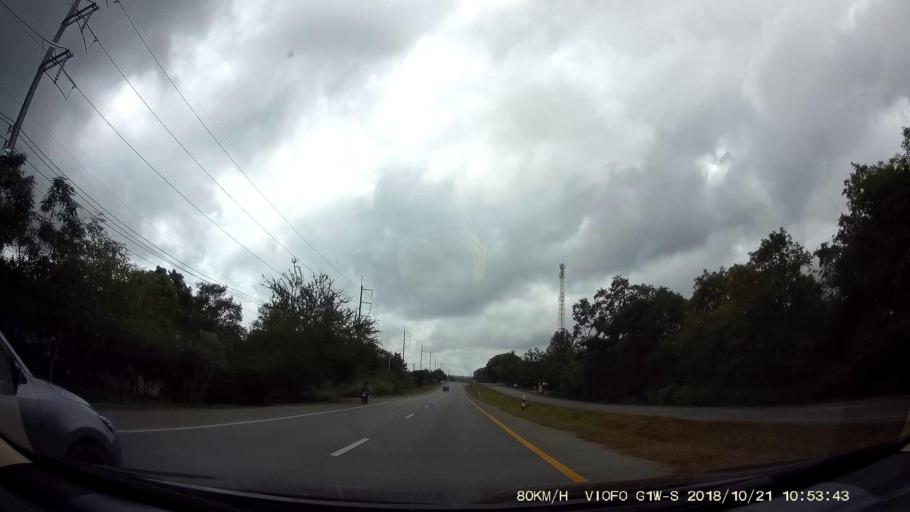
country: TH
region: Chaiyaphum
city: Khon Sawan
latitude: 15.9618
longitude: 102.1802
